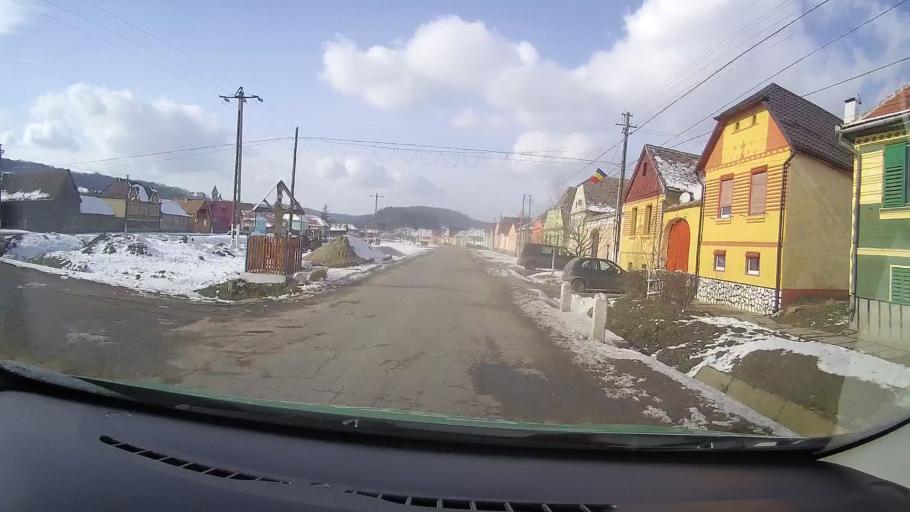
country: RO
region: Sibiu
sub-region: Comuna Iacobeni
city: Iacobeni
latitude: 46.0484
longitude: 24.7212
